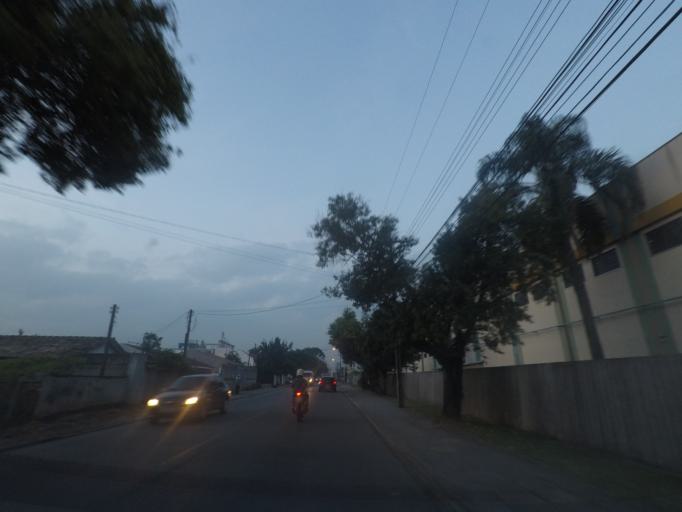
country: BR
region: Parana
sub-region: Pinhais
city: Pinhais
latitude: -25.4531
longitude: -49.1908
